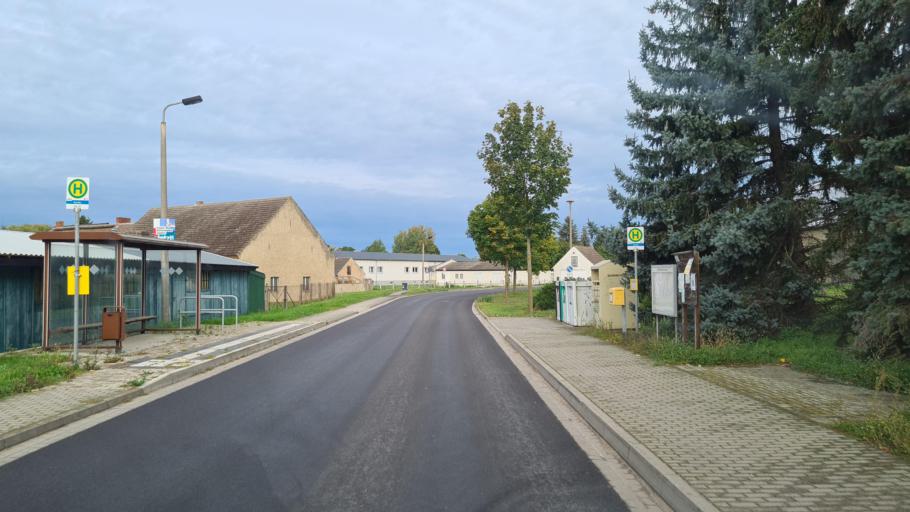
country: DE
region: Brandenburg
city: Luckau
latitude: 51.8703
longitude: 13.7249
